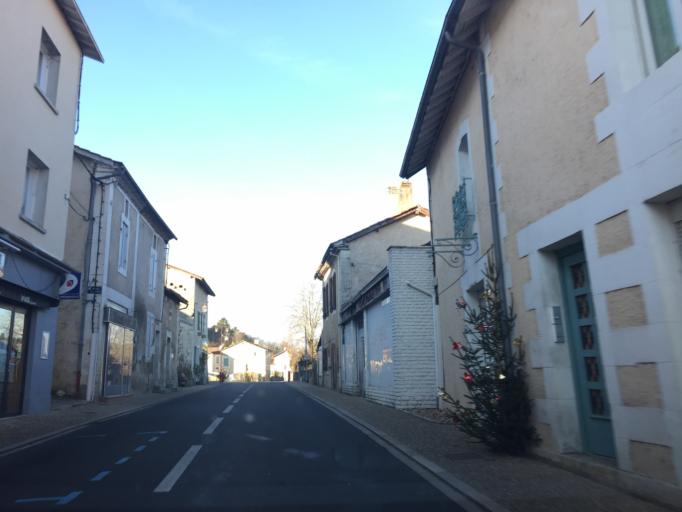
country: FR
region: Aquitaine
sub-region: Departement de la Dordogne
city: Neuvic
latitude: 45.1637
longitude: 0.3972
